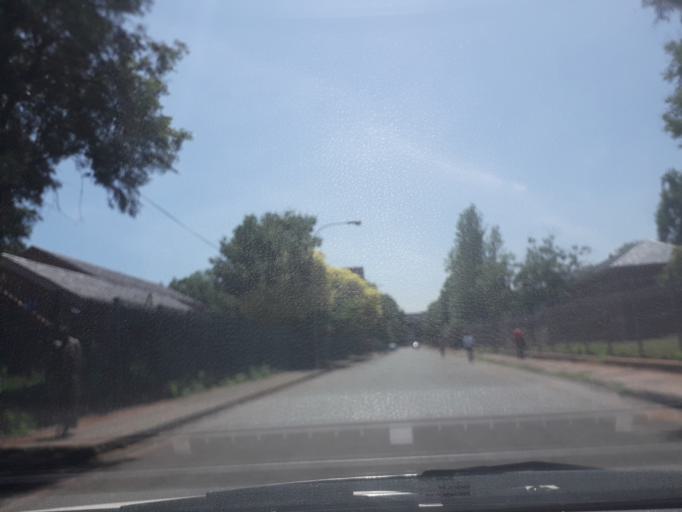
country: ZA
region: Gauteng
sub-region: City of Johannesburg Metropolitan Municipality
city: Johannesburg
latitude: -26.1844
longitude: 28.0506
